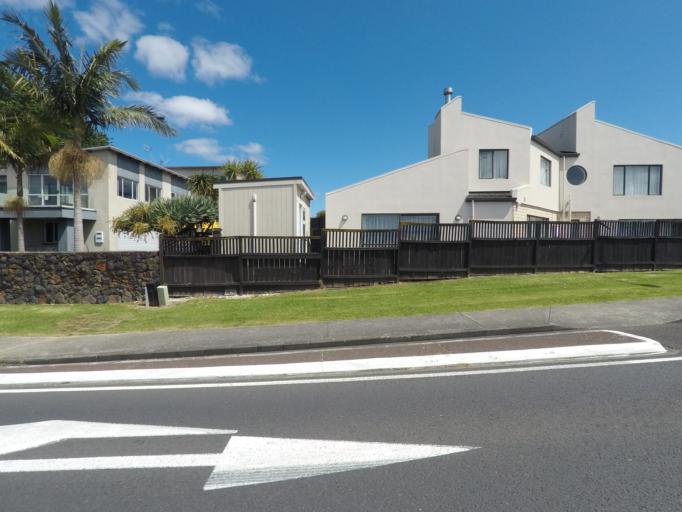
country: NZ
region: Auckland
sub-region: Auckland
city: Rosebank
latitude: -36.8496
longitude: 174.6512
